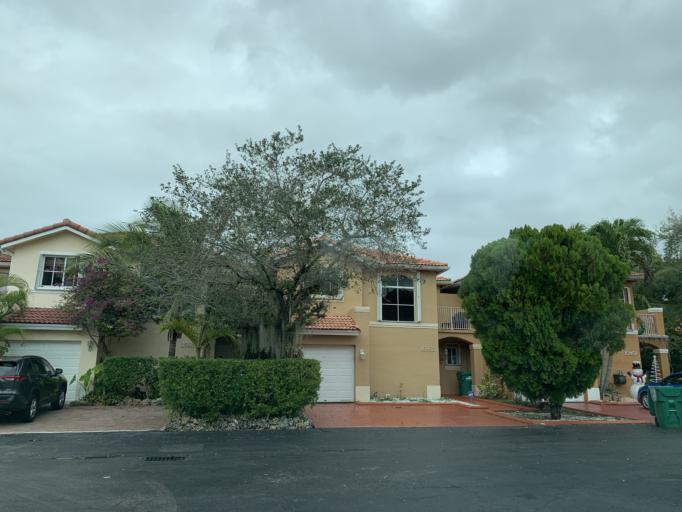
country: US
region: Florida
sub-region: Miami-Dade County
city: The Hammocks
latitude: 25.6857
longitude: -80.4497
